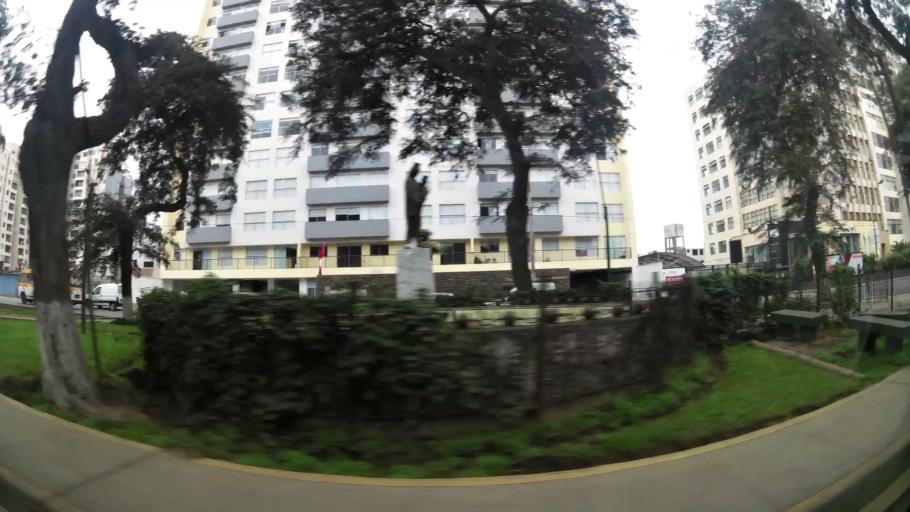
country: PE
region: Lima
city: Lima
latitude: -12.0707
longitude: -77.0406
